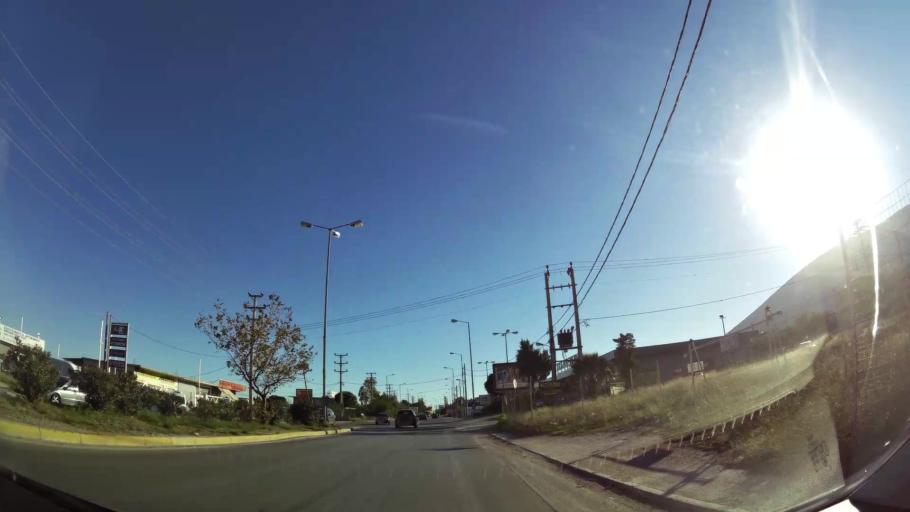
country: GR
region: Attica
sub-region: Nomarchia Anatolikis Attikis
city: Paiania
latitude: 37.9693
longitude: 23.8532
